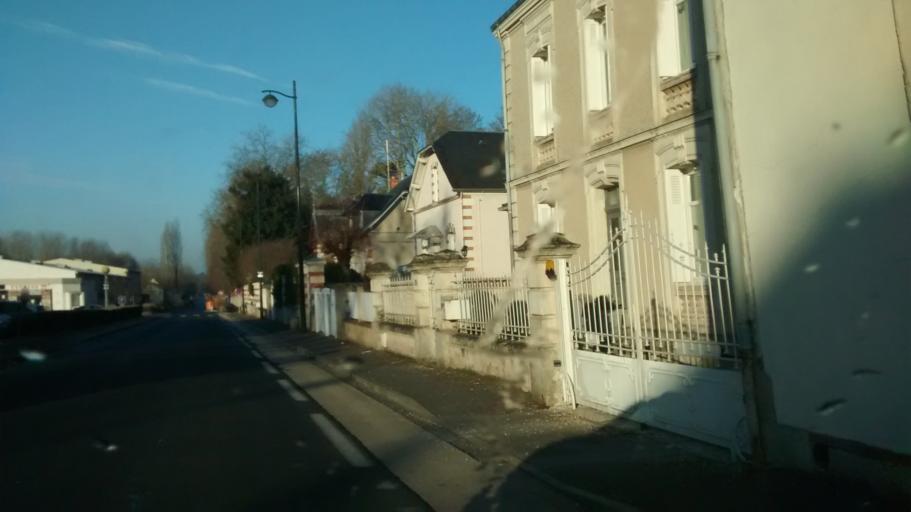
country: FR
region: Centre
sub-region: Departement d'Indre-et-Loire
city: Esvres
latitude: 47.2846
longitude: 0.7818
